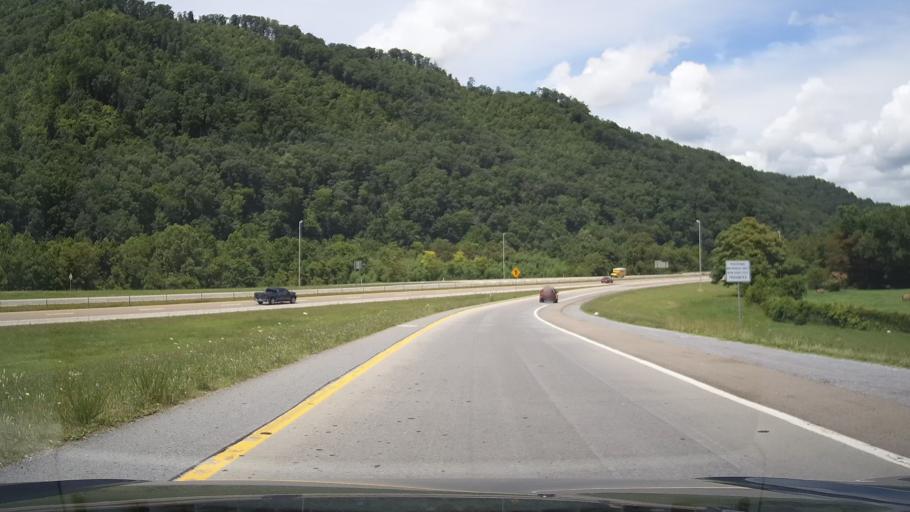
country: US
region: Tennessee
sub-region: Unicoi County
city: Banner Hill
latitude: 36.1234
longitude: -82.4453
